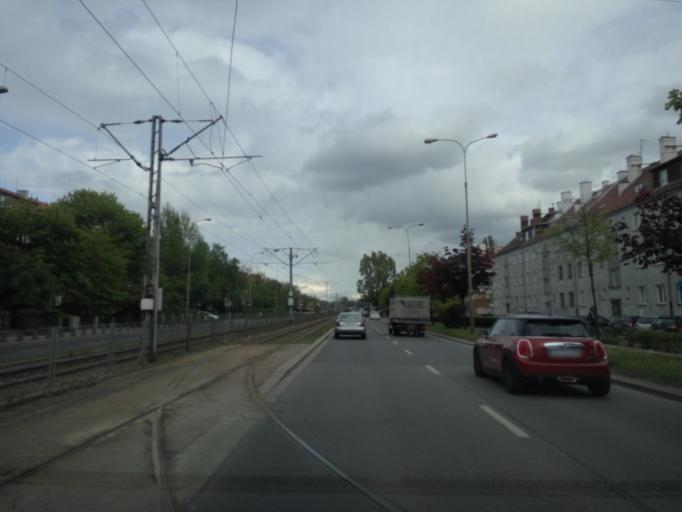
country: PL
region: Lower Silesian Voivodeship
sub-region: Powiat wroclawski
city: Wroclaw
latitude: 51.0909
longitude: 16.9891
